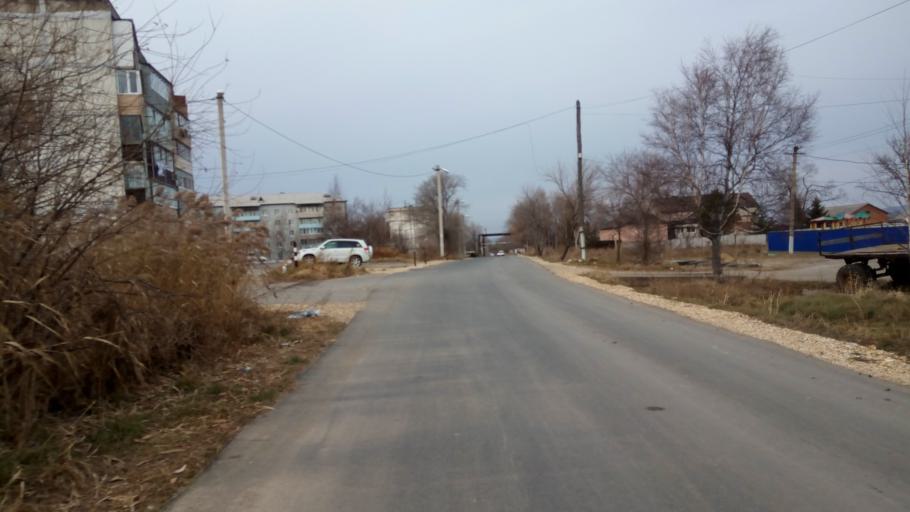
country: RU
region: Primorskiy
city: Novoshakhtinskiy
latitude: 44.0243
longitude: 132.1735
